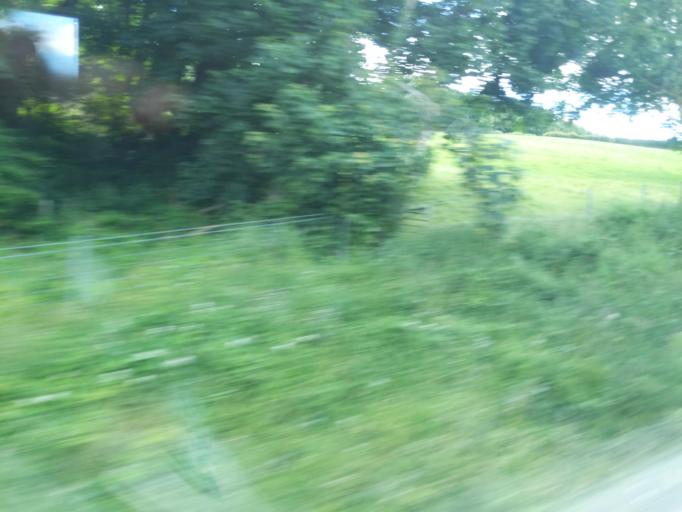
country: GB
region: England
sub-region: Cornwall
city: Liskeard
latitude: 50.4287
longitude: -4.4133
